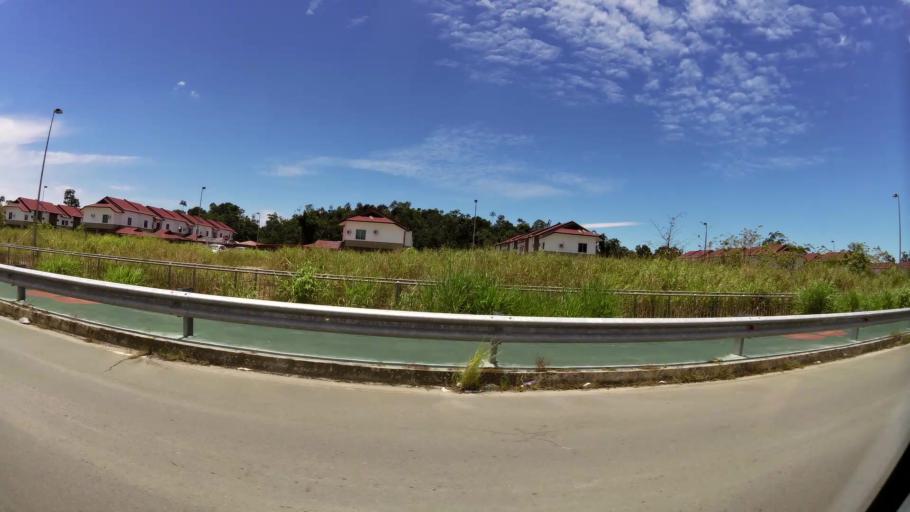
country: BN
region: Brunei and Muara
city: Bandar Seri Begawan
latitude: 5.0103
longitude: 115.0237
